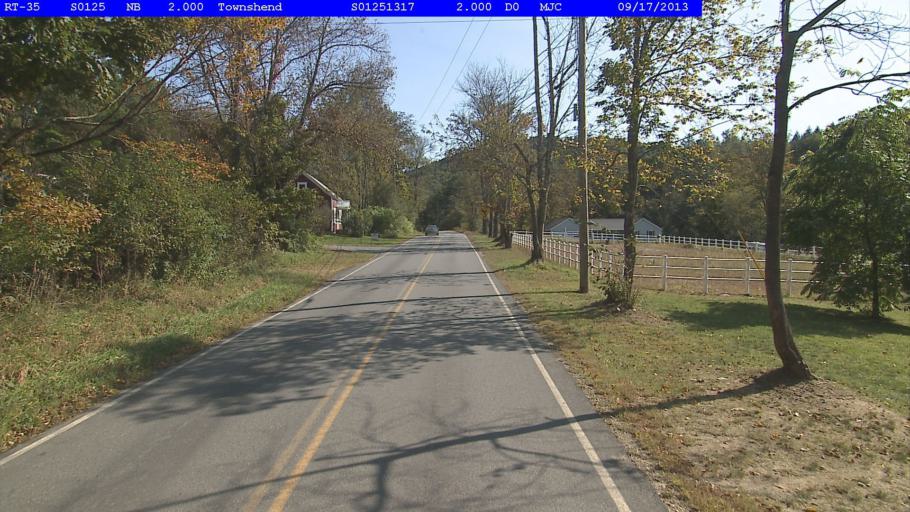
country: US
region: Vermont
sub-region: Windham County
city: Newfane
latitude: 43.0712
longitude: -72.6533
